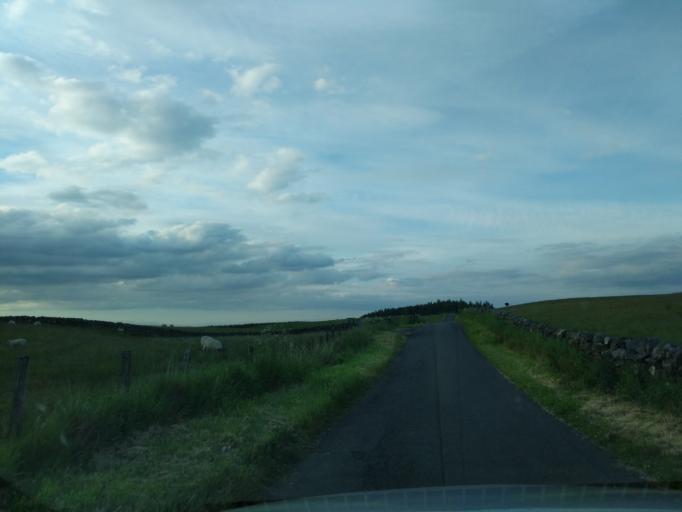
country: GB
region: Scotland
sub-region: Midlothian
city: Gorebridge
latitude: 55.7791
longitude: -3.1012
